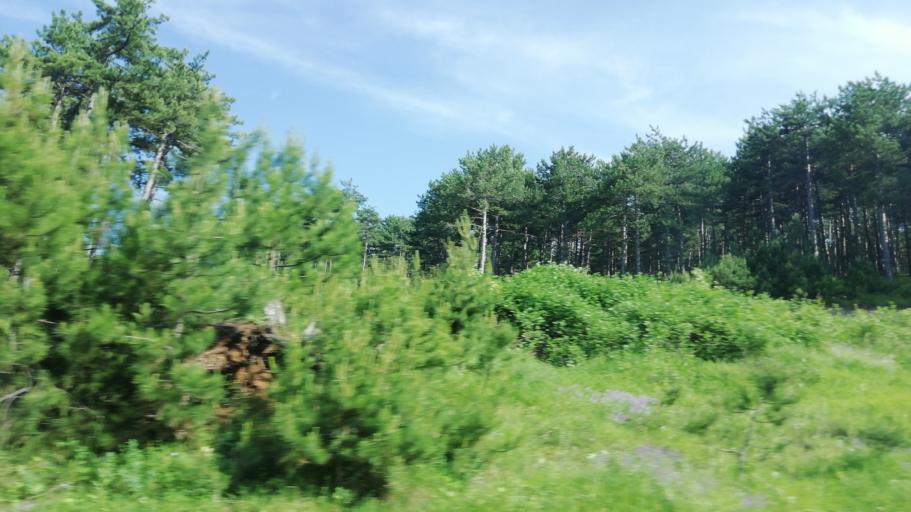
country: TR
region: Karabuk
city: Karabuk
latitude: 41.1166
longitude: 32.6037
